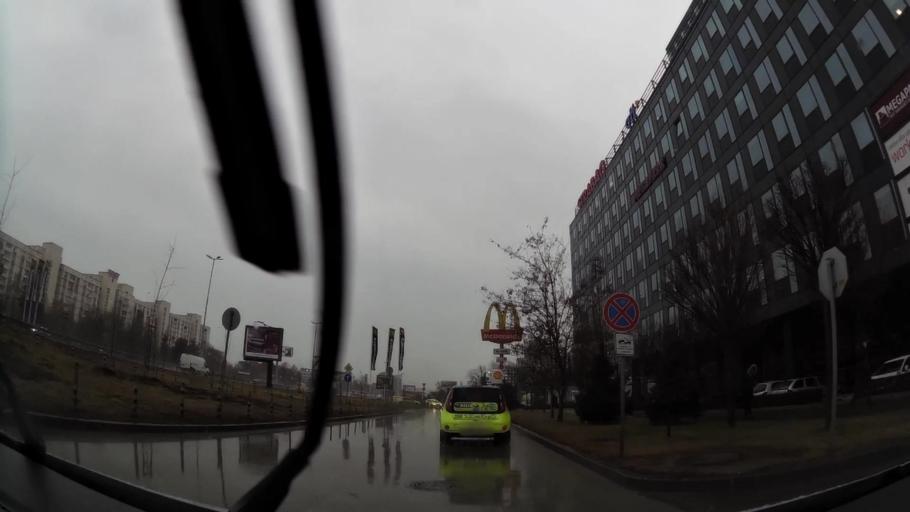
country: BG
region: Sofia-Capital
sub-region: Stolichna Obshtina
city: Sofia
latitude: 42.6609
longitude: 23.3799
